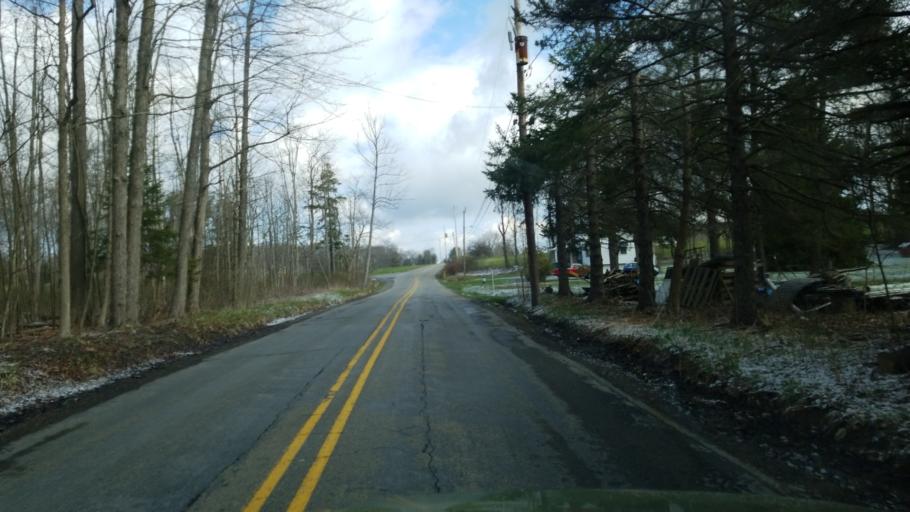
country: US
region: Pennsylvania
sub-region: Jefferson County
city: Brockway
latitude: 41.2701
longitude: -78.8426
